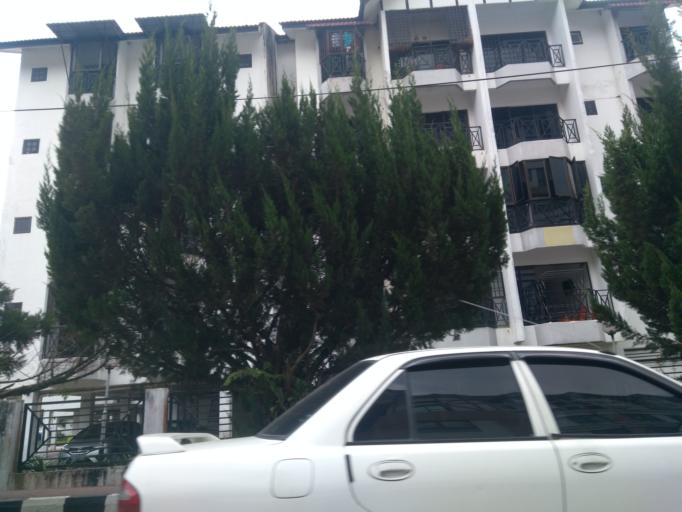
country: MY
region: Pahang
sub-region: Cameron Highlands
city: Tanah Rata
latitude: 4.4692
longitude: 101.3751
